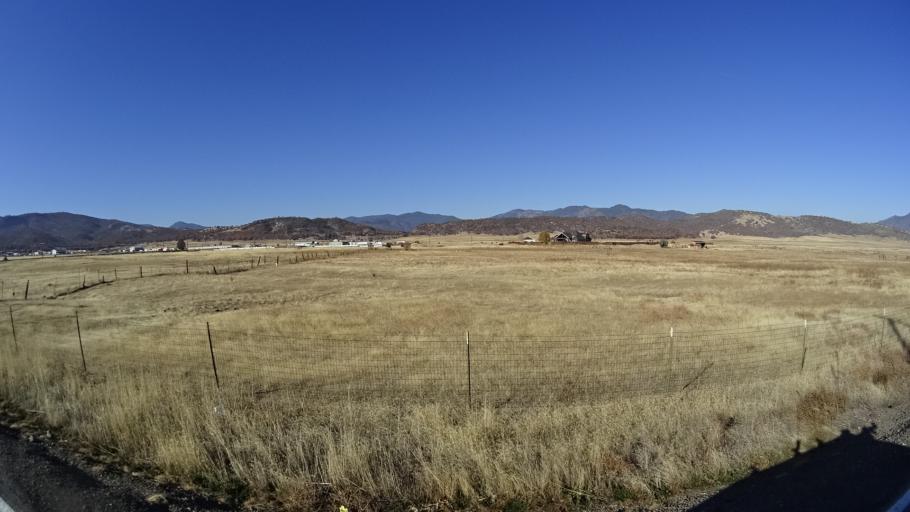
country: US
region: California
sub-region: Siskiyou County
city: Yreka
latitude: 41.7132
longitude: -122.5936
